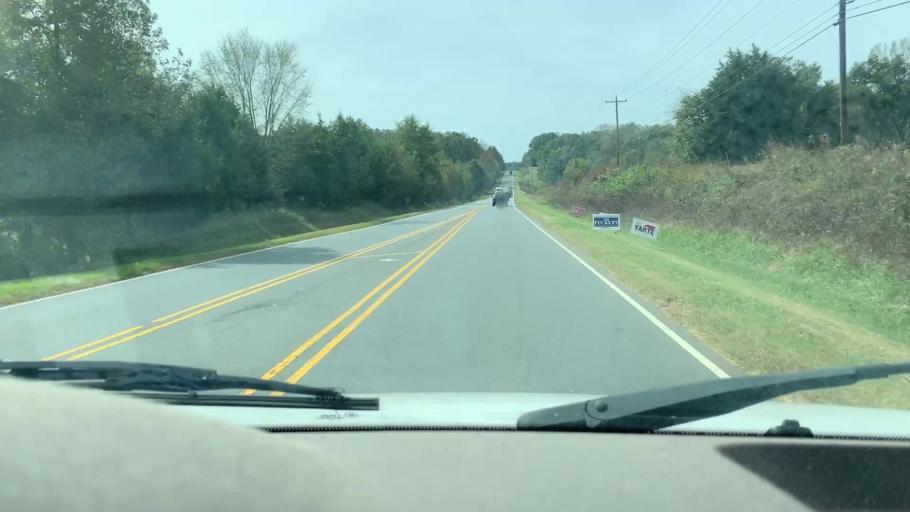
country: US
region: North Carolina
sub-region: Mecklenburg County
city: Huntersville
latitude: 35.4539
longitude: -80.8112
